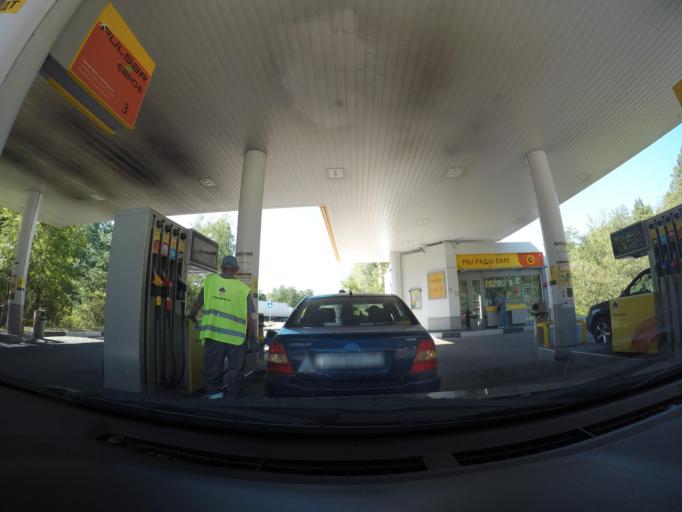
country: RU
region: Moskovskaya
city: Ramenskoye
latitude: 55.6338
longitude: 38.2765
